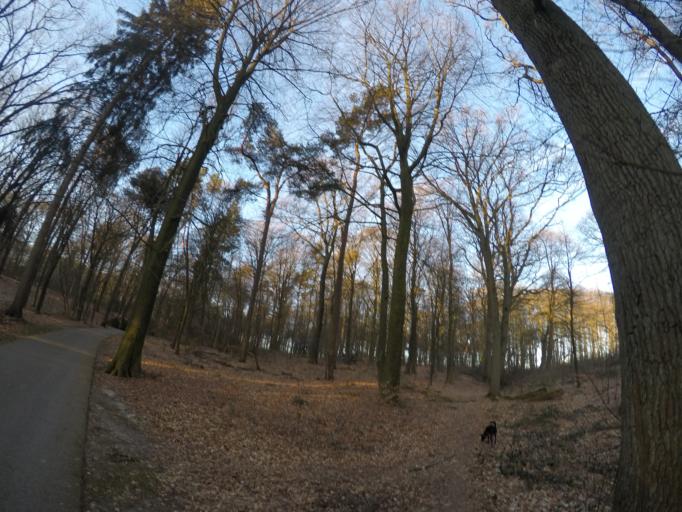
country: NL
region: Gelderland
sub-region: Gemeente Arnhem
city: Burgemeesterswijk
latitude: 51.9896
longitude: 5.8970
